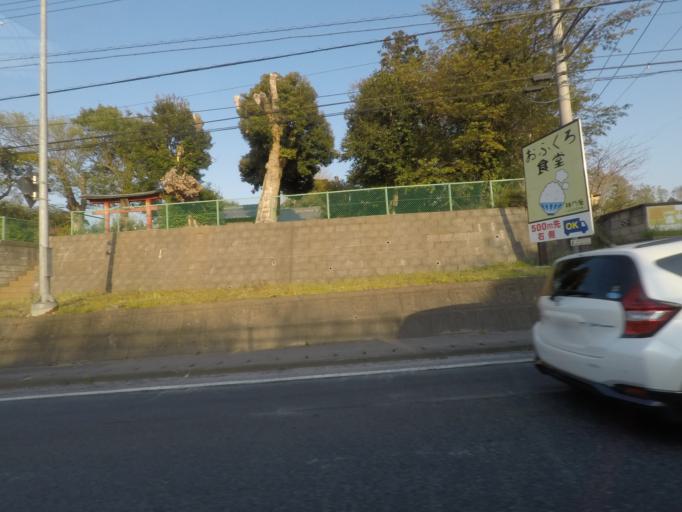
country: JP
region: Chiba
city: Sakura
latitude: 35.6752
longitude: 140.2351
